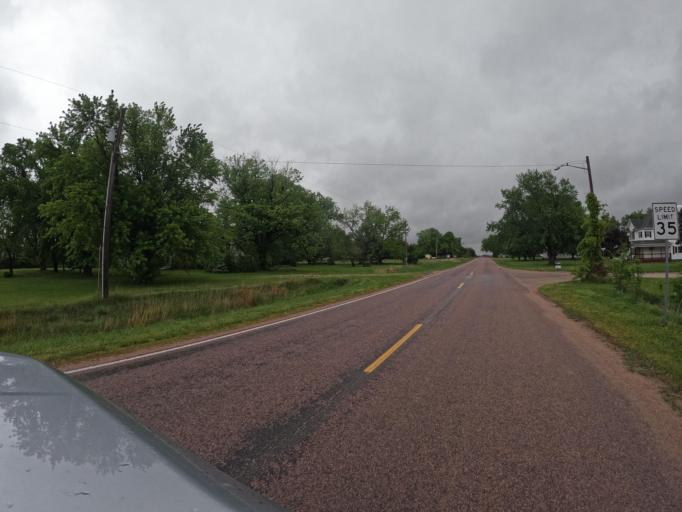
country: US
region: Nebraska
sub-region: Clay County
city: Harvard
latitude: 40.6260
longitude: -98.0989
